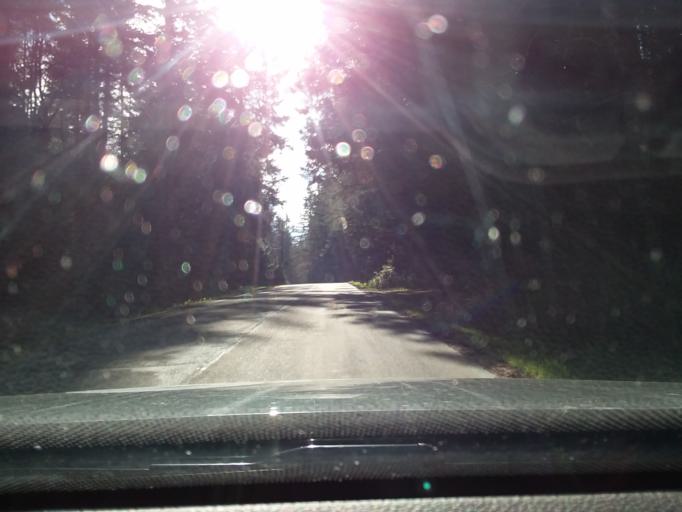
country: CA
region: British Columbia
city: North Cowichan
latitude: 48.9232
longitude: -123.4456
